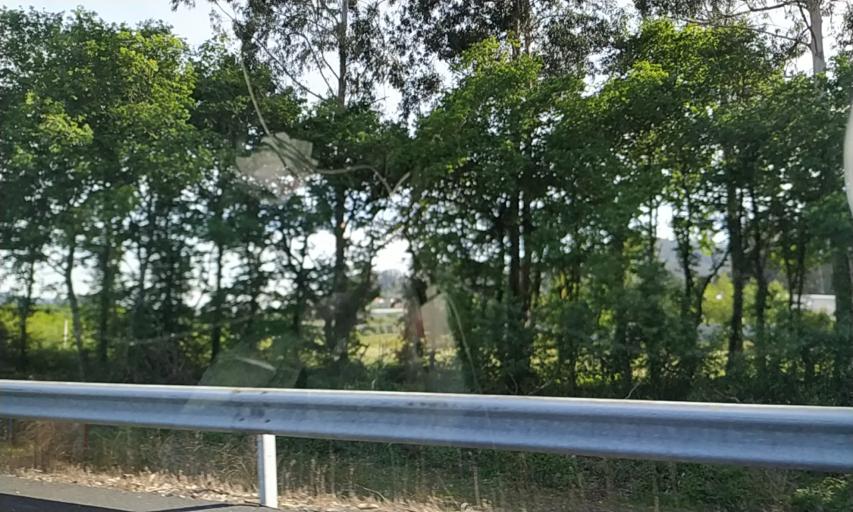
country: ES
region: Galicia
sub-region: Provincia de Pontevedra
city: Pontevedra
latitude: 42.4674
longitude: -8.6535
